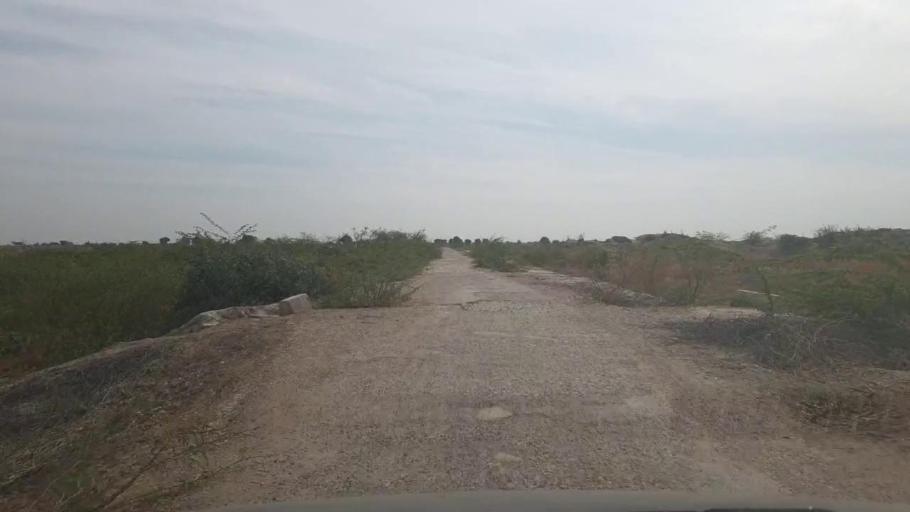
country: PK
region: Sindh
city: Kunri
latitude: 25.2413
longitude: 69.6062
